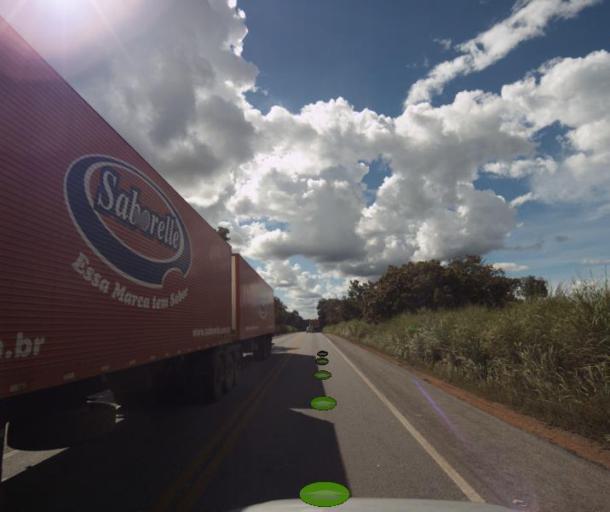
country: BR
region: Goias
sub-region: Porangatu
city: Porangatu
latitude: -13.2091
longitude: -49.1535
